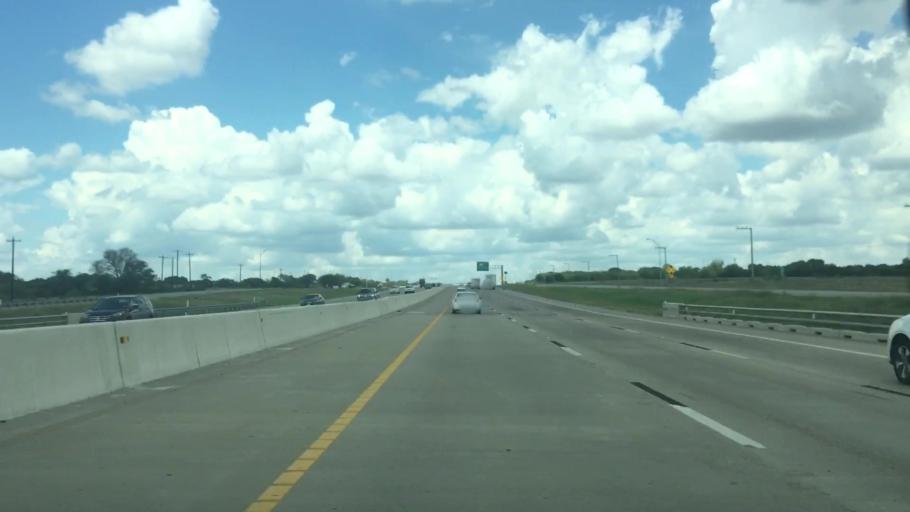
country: US
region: Texas
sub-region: McLennan County
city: Lorena
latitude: 31.3696
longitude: -97.2159
